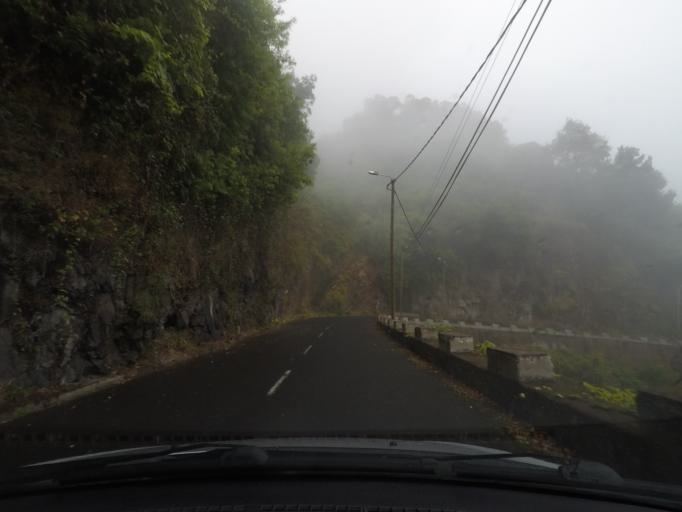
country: PT
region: Madeira
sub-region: Santana
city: Santana
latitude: 32.7778
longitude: -16.8638
